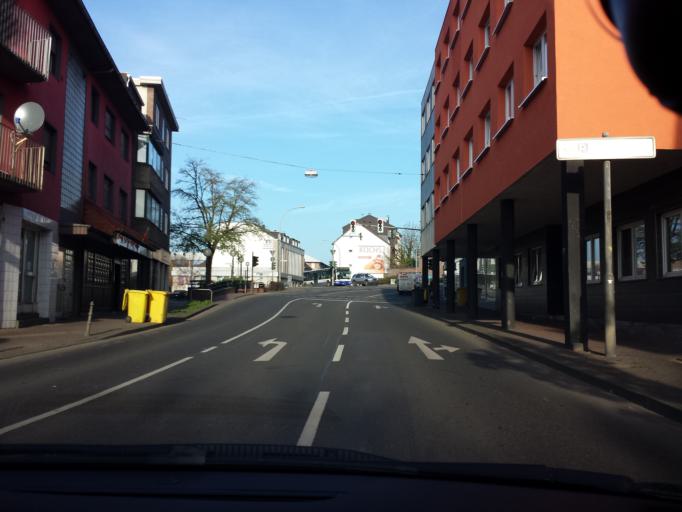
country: DE
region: North Rhine-Westphalia
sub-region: Regierungsbezirk Koln
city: Herzogenrath
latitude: 50.8685
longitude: 6.0968
